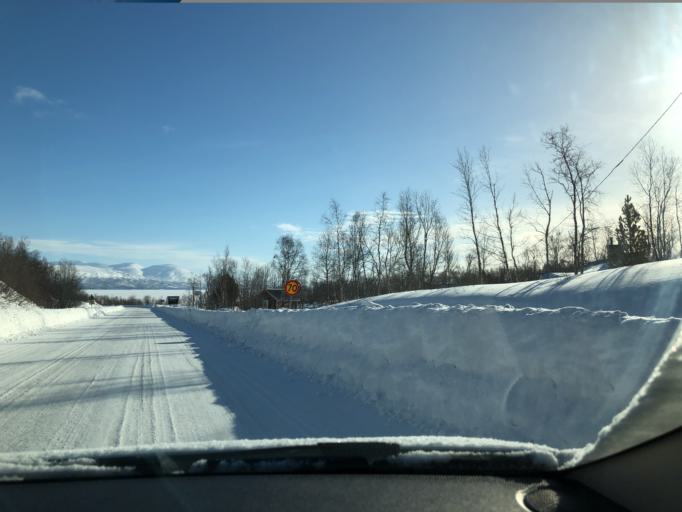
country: NO
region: Troms
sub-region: Bardu
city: Setermoen
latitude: 68.4029
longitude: 18.6852
